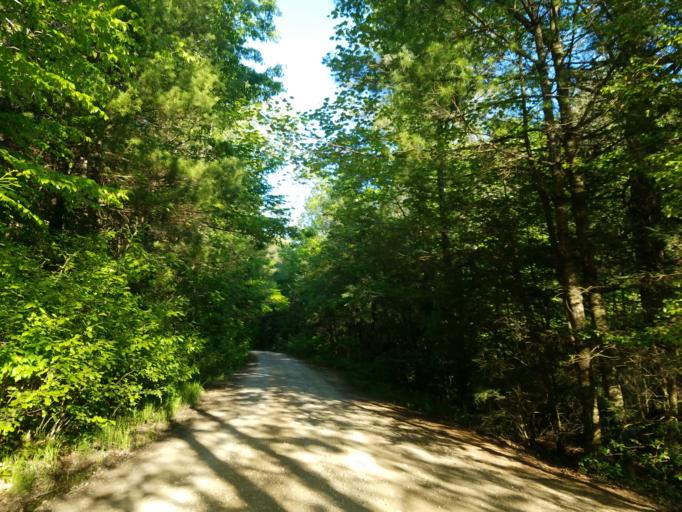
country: US
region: Georgia
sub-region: Lumpkin County
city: Dahlonega
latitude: 34.6811
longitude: -84.1390
